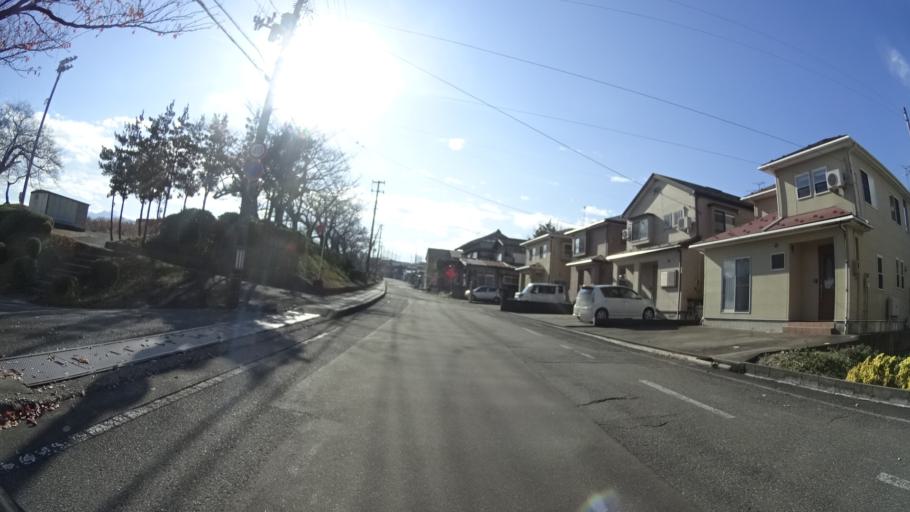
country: JP
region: Niigata
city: Itoigawa
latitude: 37.0336
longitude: 137.8582
